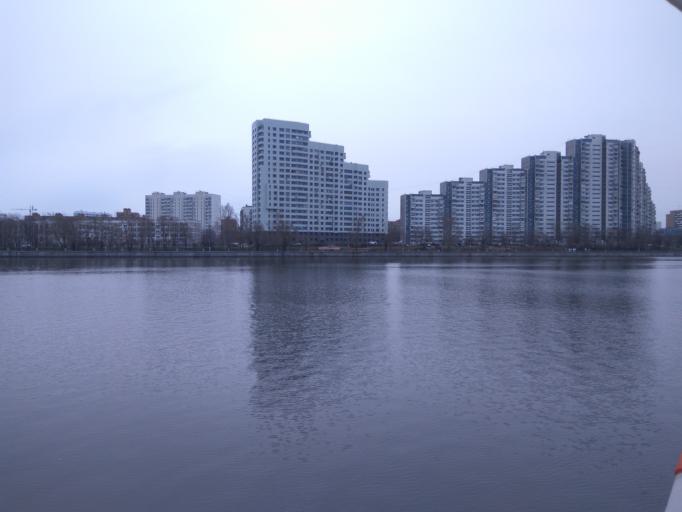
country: RU
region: Moskovskaya
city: Kozhukhovo
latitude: 55.6923
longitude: 37.6857
